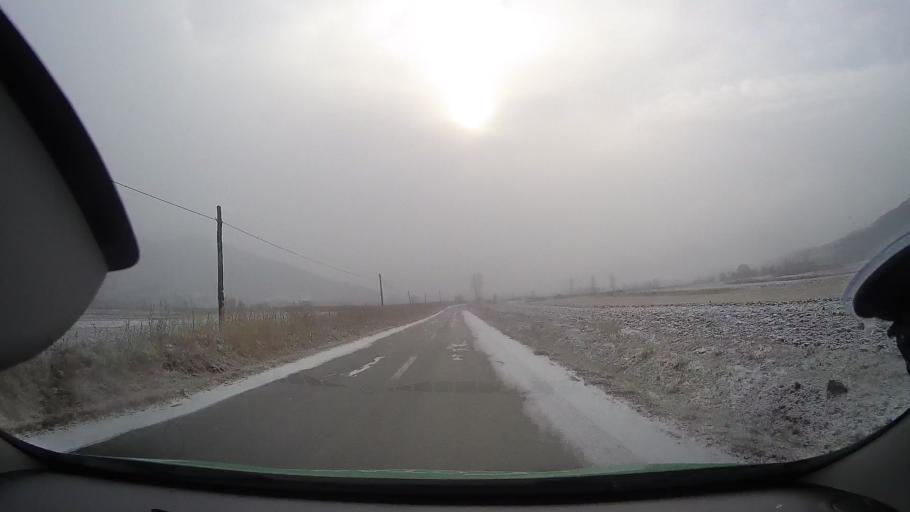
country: RO
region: Alba
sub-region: Comuna Rimetea
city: Rimetea
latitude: 46.4126
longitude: 23.5584
